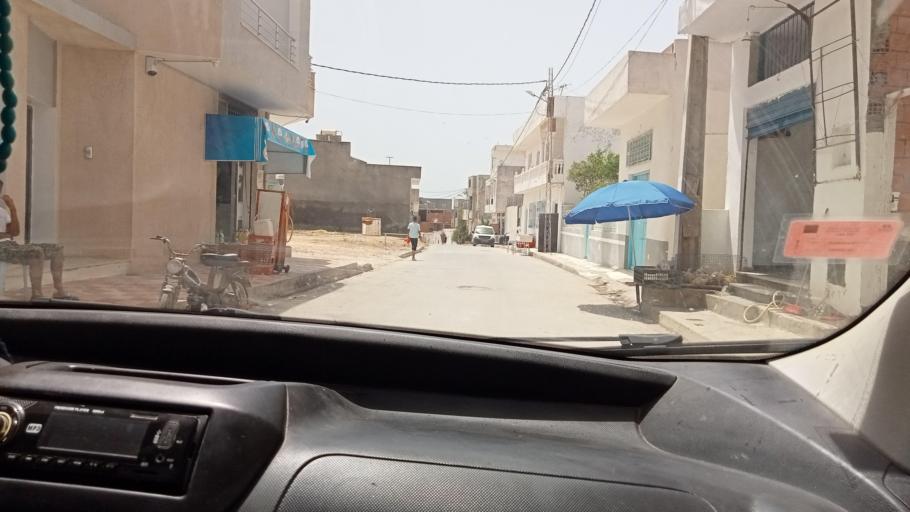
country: TN
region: Nabul
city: Qulaybiyah
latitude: 36.8541
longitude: 11.0884
